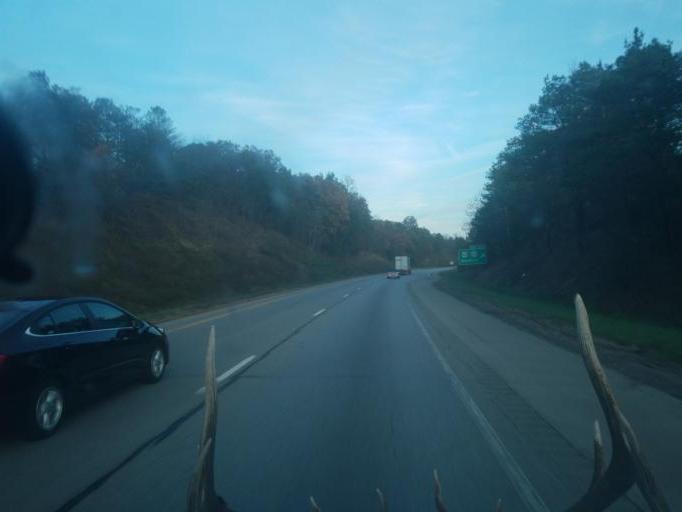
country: US
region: Ohio
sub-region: Muskingum County
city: New Concord
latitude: 39.9760
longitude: -81.8420
